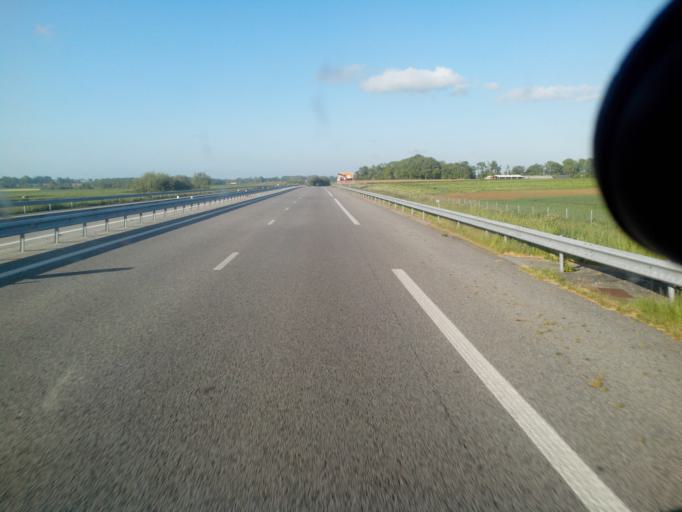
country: FR
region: Haute-Normandie
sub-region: Departement de la Seine-Maritime
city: Sainte-Marie-des-Champs
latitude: 49.6512
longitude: 0.7918
